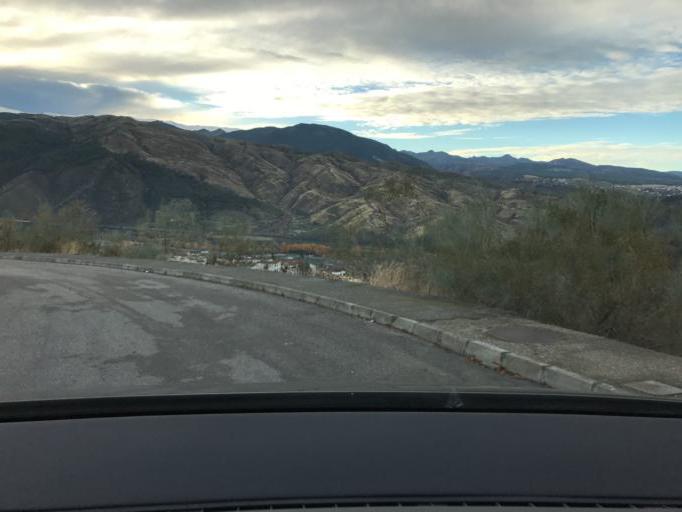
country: ES
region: Andalusia
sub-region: Provincia de Granada
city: Cenes de la Vega
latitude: 37.1669
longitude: -3.5447
